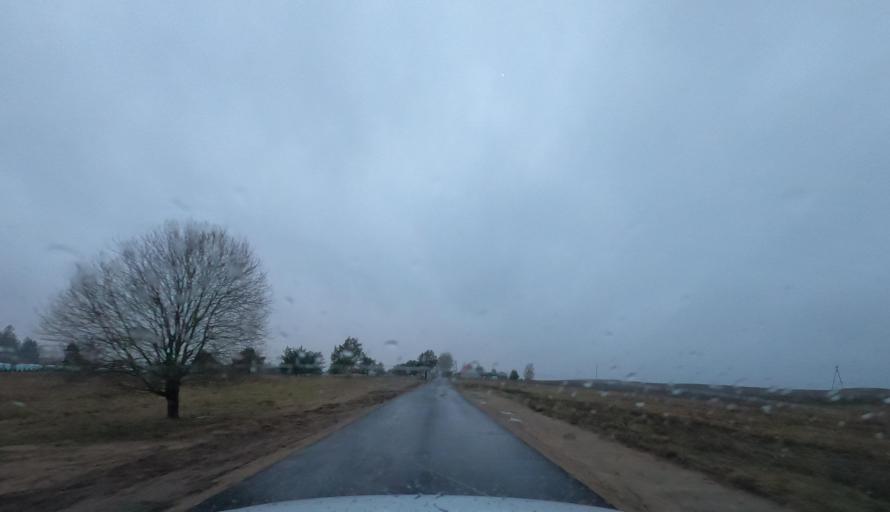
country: PL
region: West Pomeranian Voivodeship
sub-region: Powiat szczecinecki
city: Szczecinek
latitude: 53.7210
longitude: 16.6065
